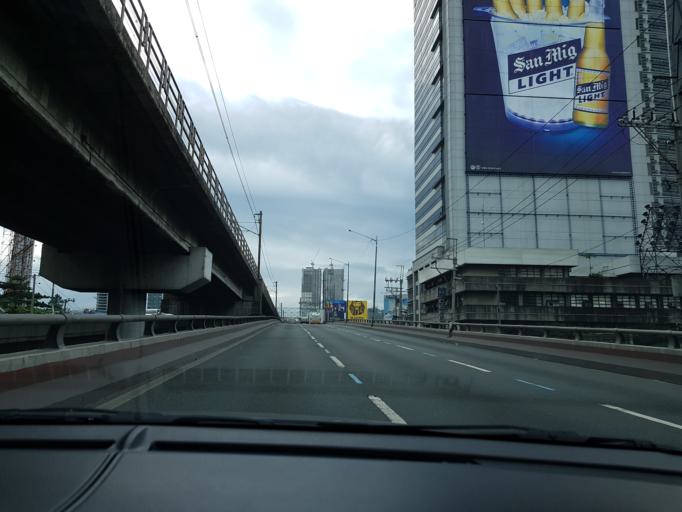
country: PH
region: Metro Manila
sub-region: Quezon City
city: Quezon City
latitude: 14.6457
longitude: 121.0365
